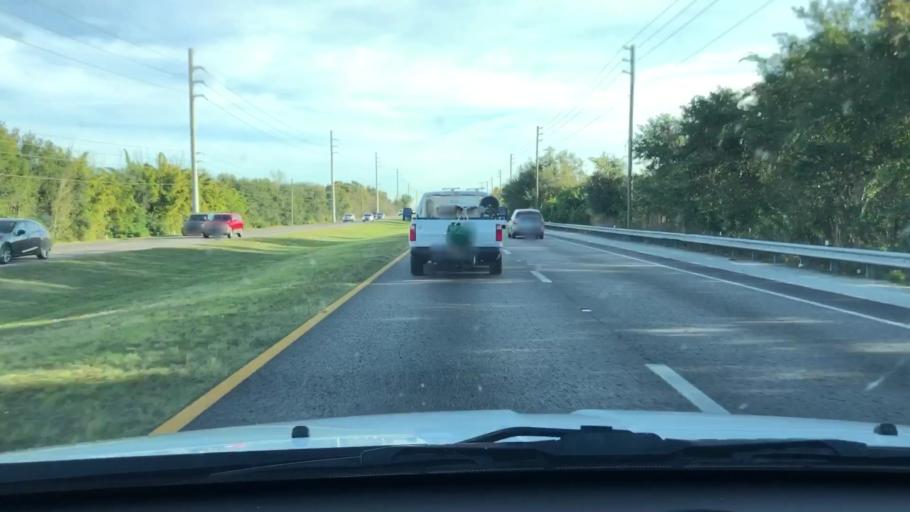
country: US
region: Florida
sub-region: Osceola County
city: Campbell
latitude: 28.2657
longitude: -81.4297
